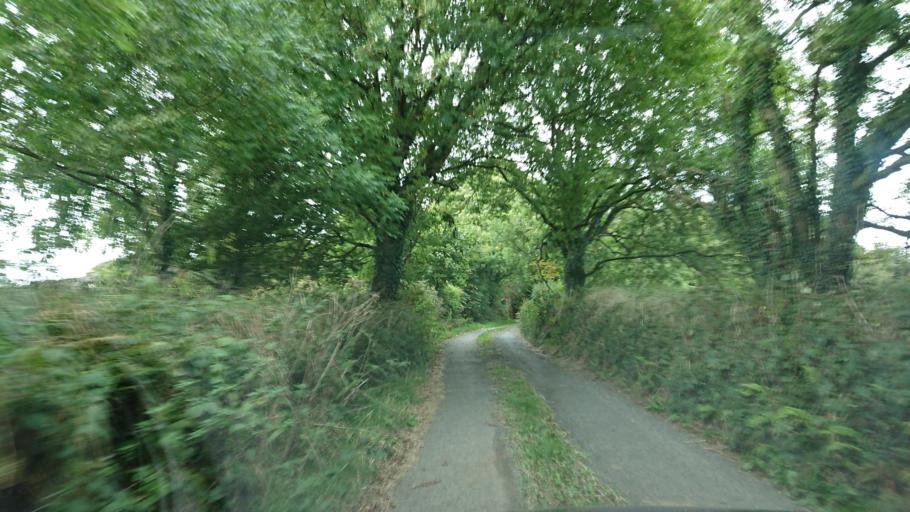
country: IE
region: Munster
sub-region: Waterford
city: Dunmore East
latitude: 52.2027
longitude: -7.0446
